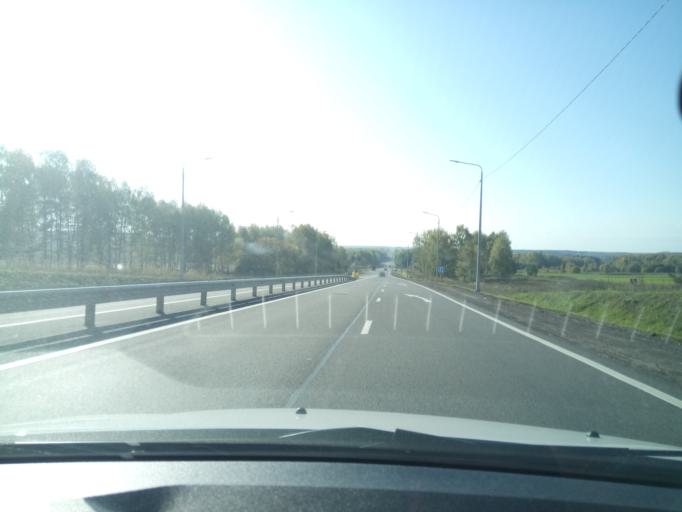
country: RU
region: Nizjnij Novgorod
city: Dal'neye Konstantinovo
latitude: 55.9929
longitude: 43.9687
